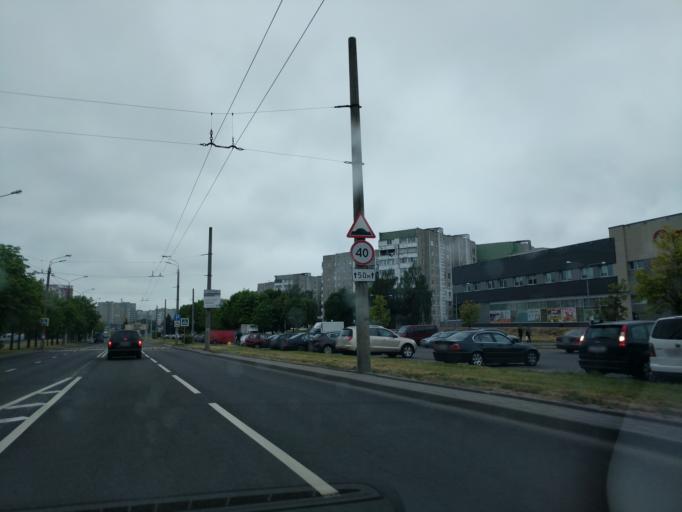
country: BY
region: Minsk
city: Novoye Medvezhino
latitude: 53.8649
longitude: 27.4686
